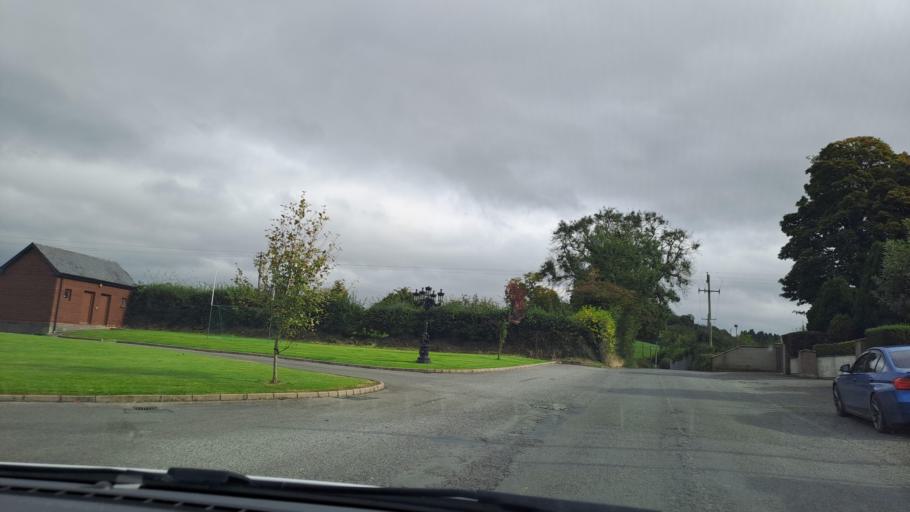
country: IE
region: Ulster
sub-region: An Cabhan
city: Bailieborough
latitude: 53.9933
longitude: -6.9282
